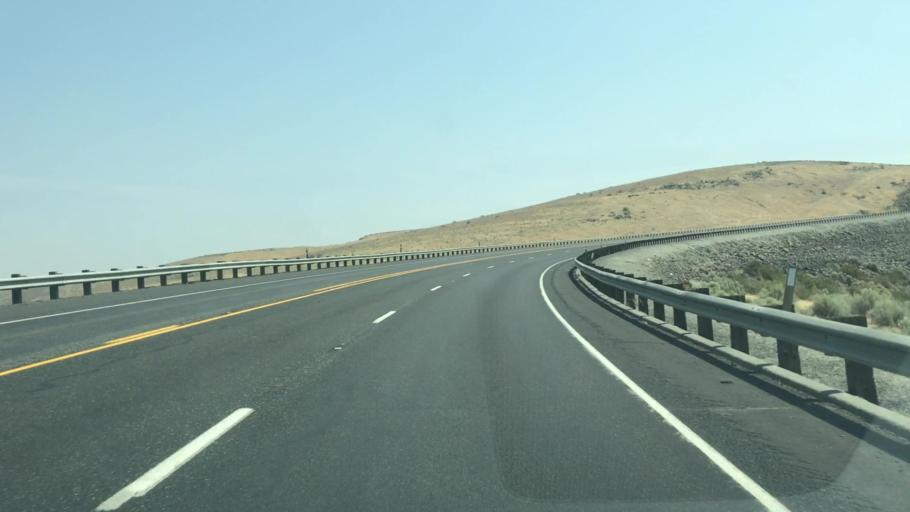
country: US
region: Washington
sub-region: Grant County
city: Quincy
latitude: 47.2428
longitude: -119.9806
